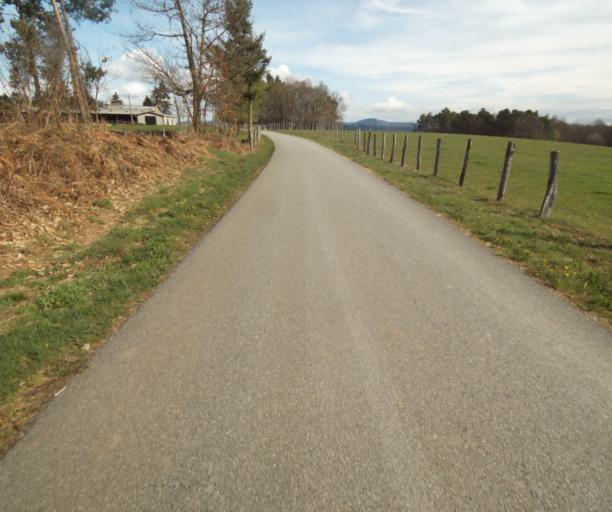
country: FR
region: Limousin
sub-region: Departement de la Correze
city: Correze
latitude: 45.3319
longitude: 1.8578
